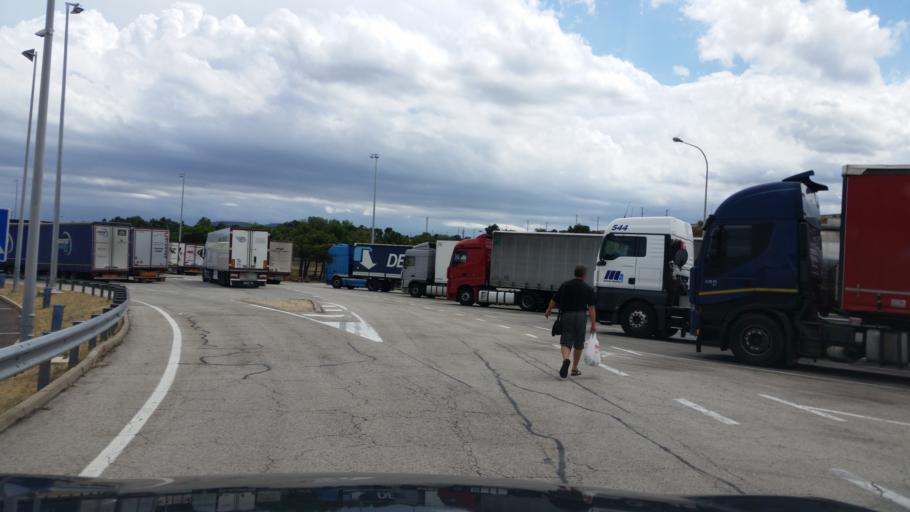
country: ES
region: Catalonia
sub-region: Provincia de Girona
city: la Jonquera
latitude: 42.4061
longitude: 2.8714
